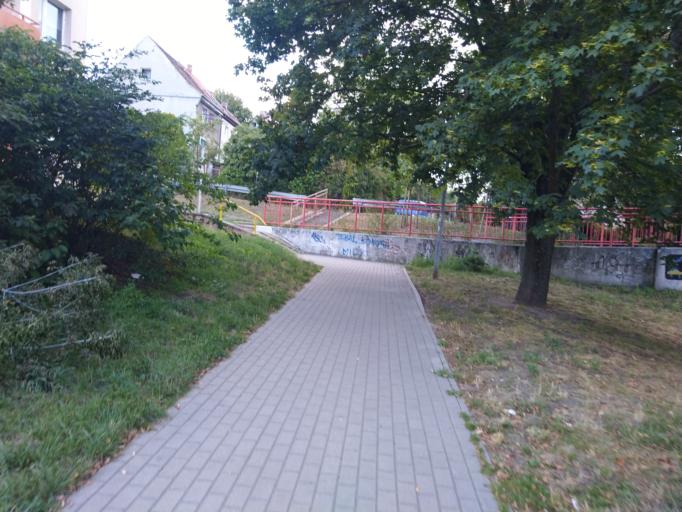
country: PL
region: West Pomeranian Voivodeship
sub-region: Szczecin
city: Szczecin
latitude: 53.4496
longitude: 14.5616
